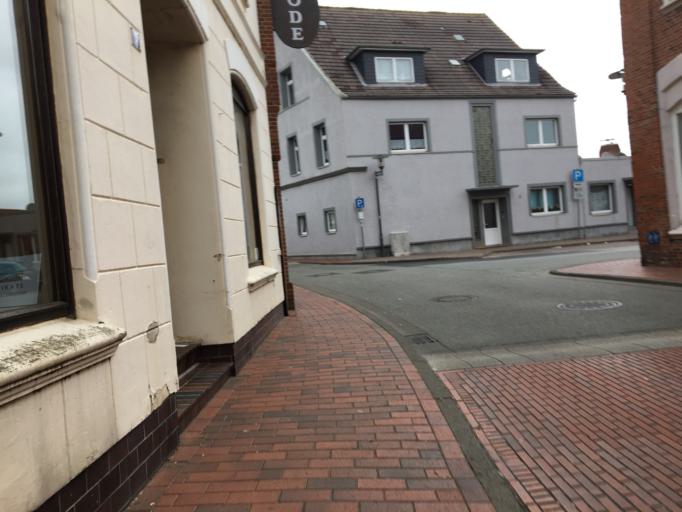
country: DE
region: Schleswig-Holstein
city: Tonning
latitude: 54.3178
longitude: 8.9422
